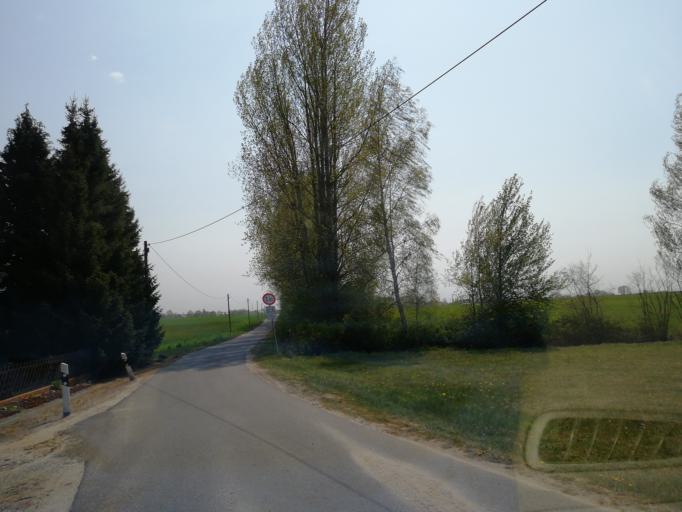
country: DE
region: Brandenburg
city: Sallgast
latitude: 51.6492
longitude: 13.8575
